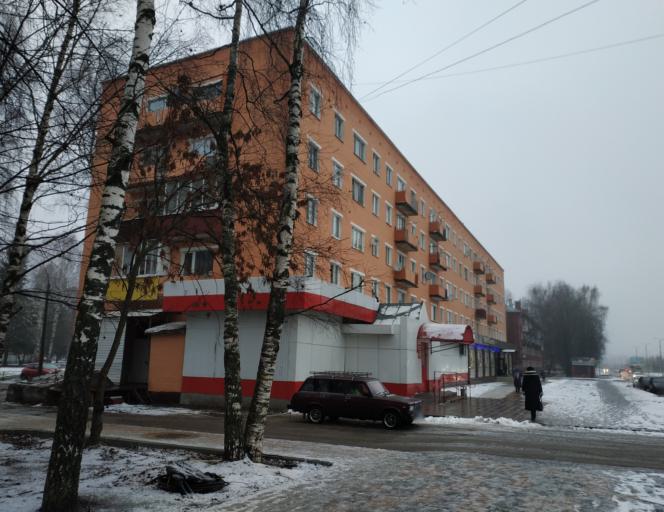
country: RU
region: Moskovskaya
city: Taldom
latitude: 56.7398
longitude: 37.5372
